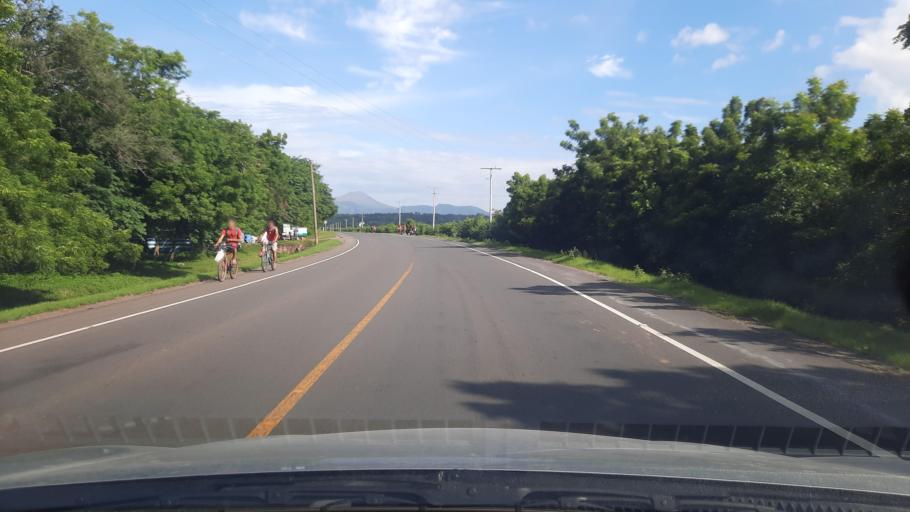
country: NI
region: Chinandega
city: Chichigalpa
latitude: 12.7555
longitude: -86.8976
